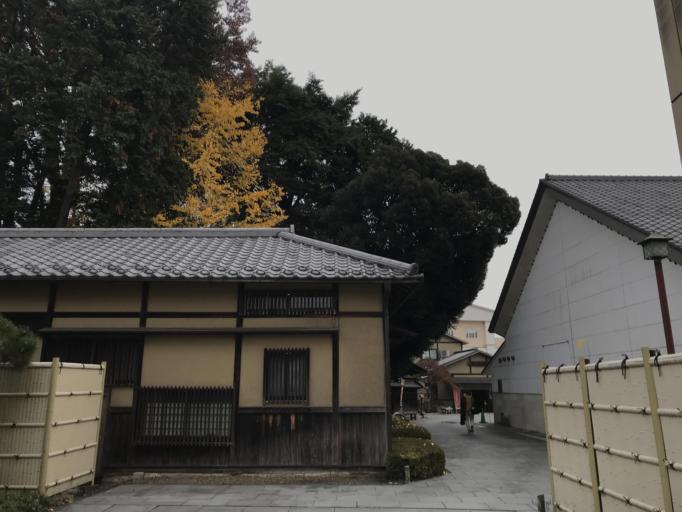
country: JP
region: Tochigi
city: Kanuma
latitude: 36.5661
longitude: 139.7474
